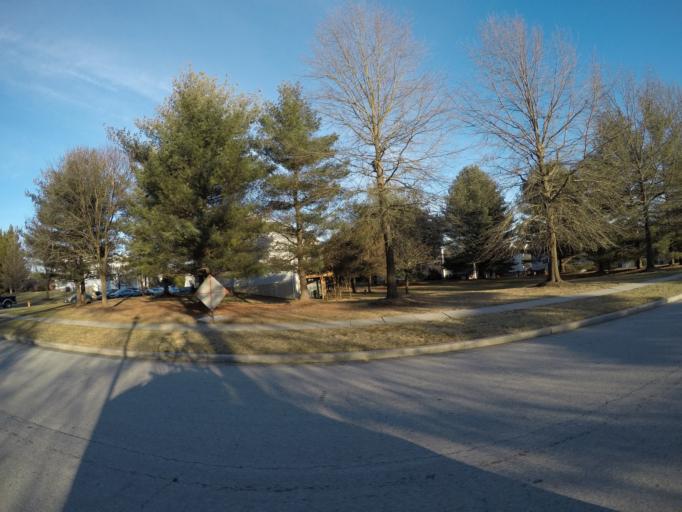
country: US
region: Maryland
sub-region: Howard County
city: Ellicott City
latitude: 39.2749
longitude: -76.8135
